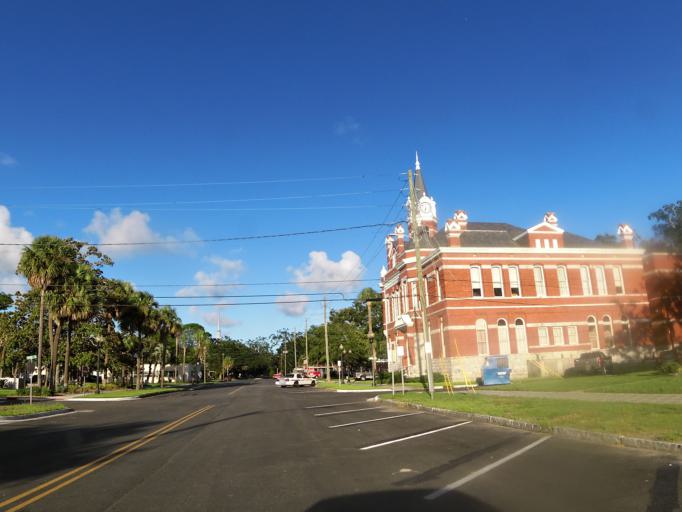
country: US
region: Georgia
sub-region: Glynn County
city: Brunswick
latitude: 31.1461
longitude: -81.4952
